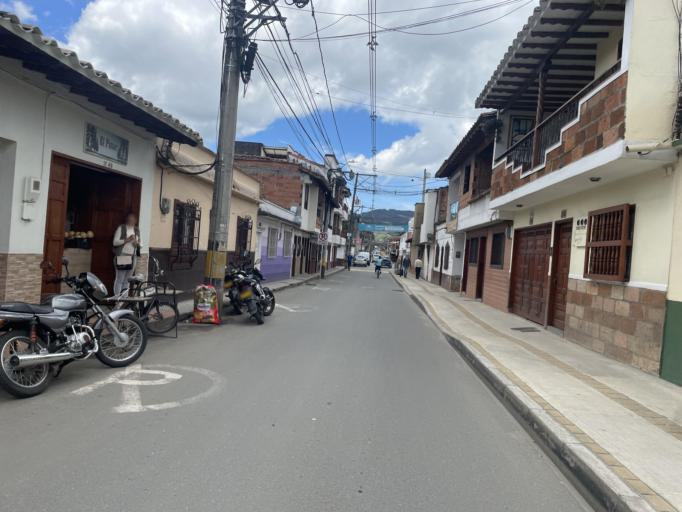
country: CO
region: Antioquia
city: La Ceja
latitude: 6.0288
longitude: -75.4309
